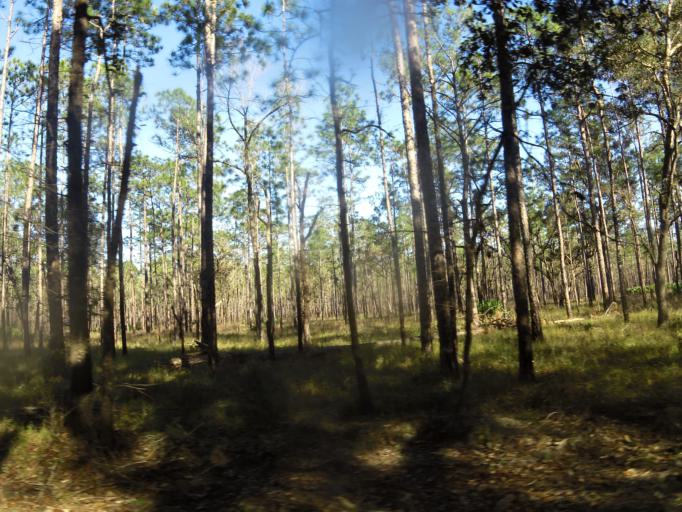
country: US
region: Florida
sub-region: Clay County
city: Middleburg
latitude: 30.1452
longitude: -81.9067
